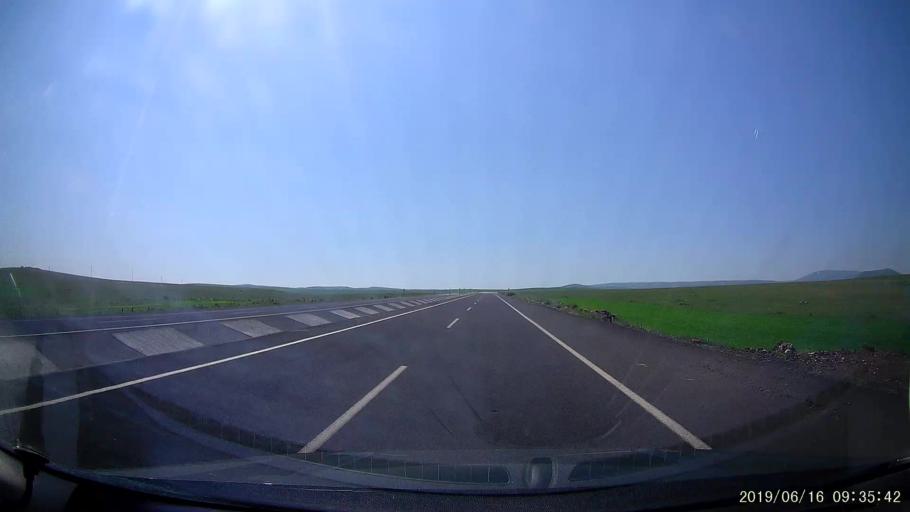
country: TR
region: Kars
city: Kars
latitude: 40.5679
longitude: 43.1601
